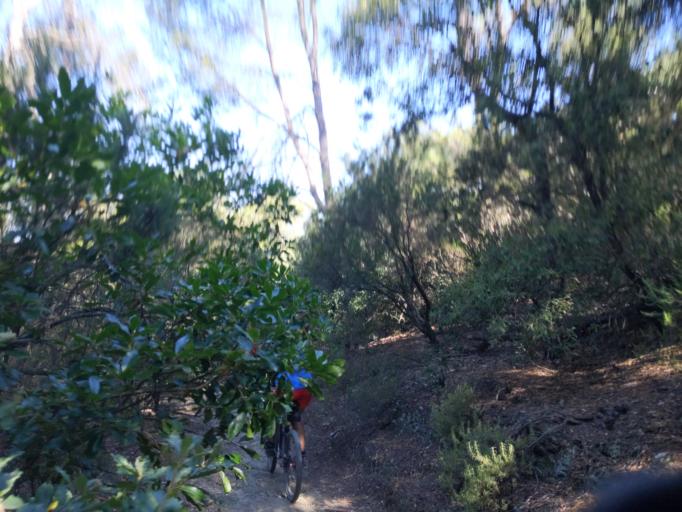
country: ES
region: Catalonia
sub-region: Provincia de Barcelona
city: Cerdanyola del Valles
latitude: 41.4674
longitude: 2.1315
